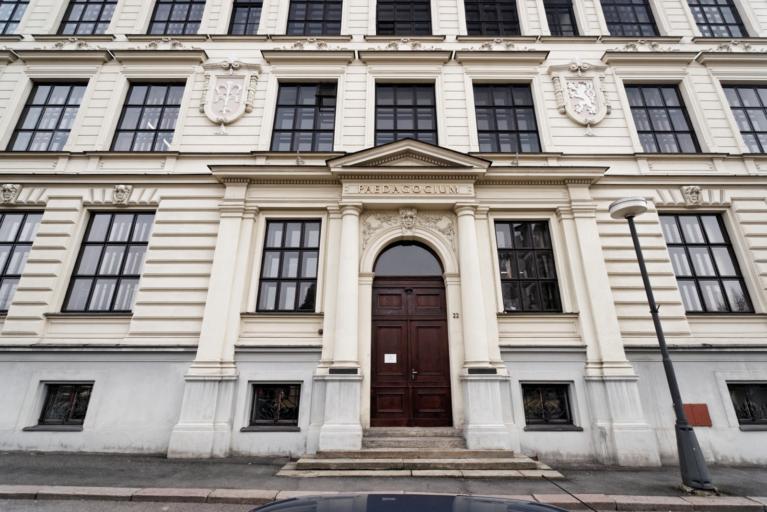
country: CZ
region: Pardubicky
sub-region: Okres Svitavy
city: Litomysl
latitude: 49.8732
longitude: 16.3088
